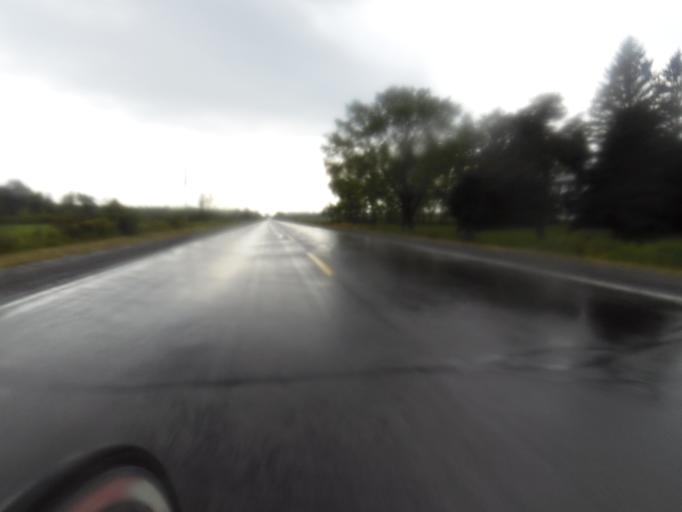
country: CA
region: Ontario
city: Bells Corners
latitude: 45.2054
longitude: -75.7182
